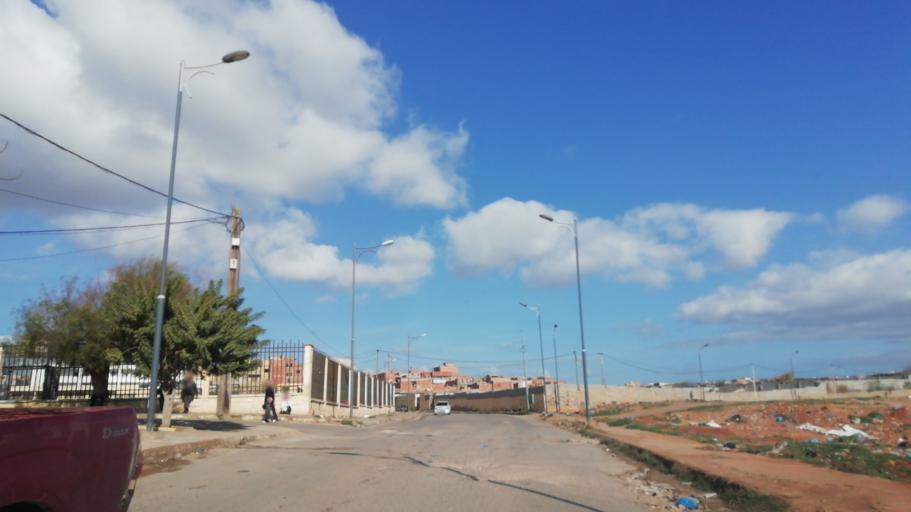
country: DZ
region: Oran
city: Es Senia
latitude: 35.6321
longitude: -0.6617
